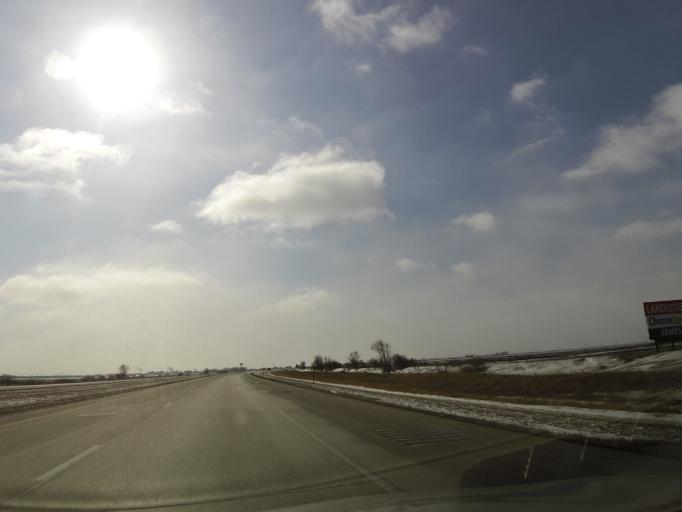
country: US
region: North Dakota
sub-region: Grand Forks County
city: Grand Forks
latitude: 47.9700
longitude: -97.0943
